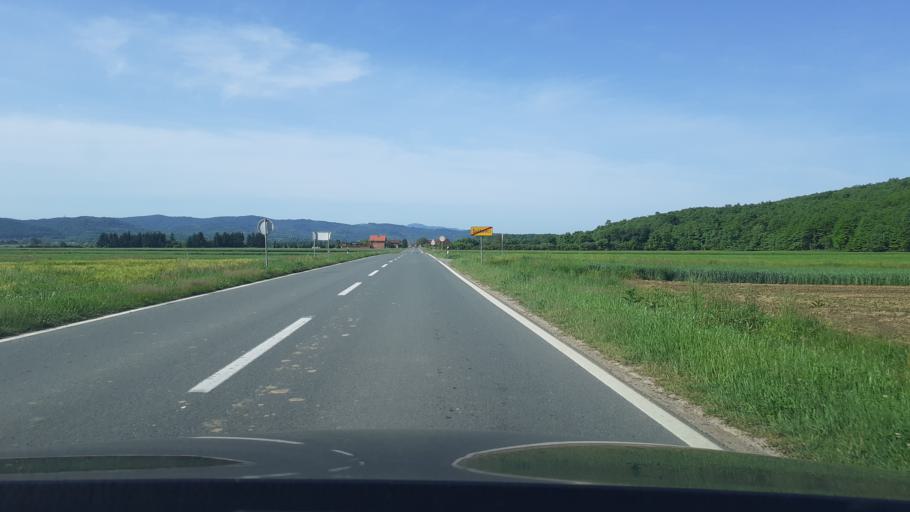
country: HR
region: Pozesko-Slavonska
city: Pleternica
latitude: 45.2583
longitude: 17.7621
